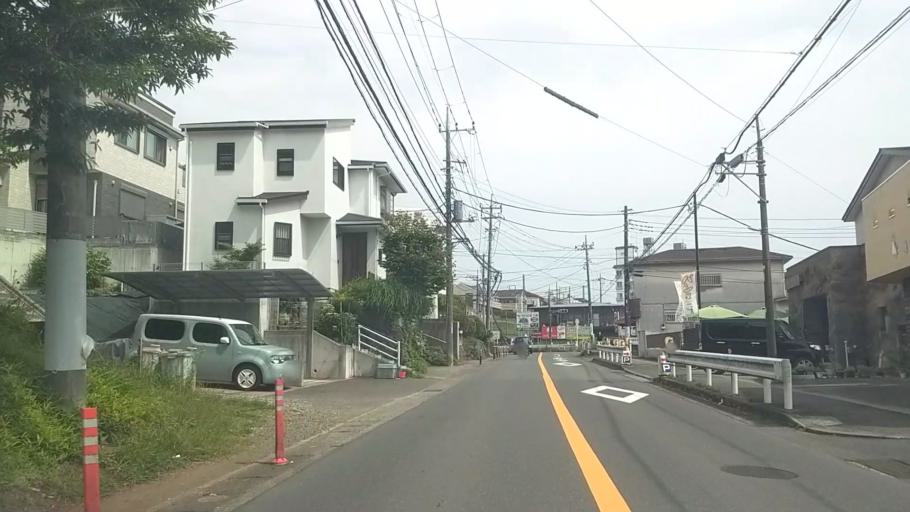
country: JP
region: Kanagawa
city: Fujisawa
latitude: 35.3871
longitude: 139.4686
